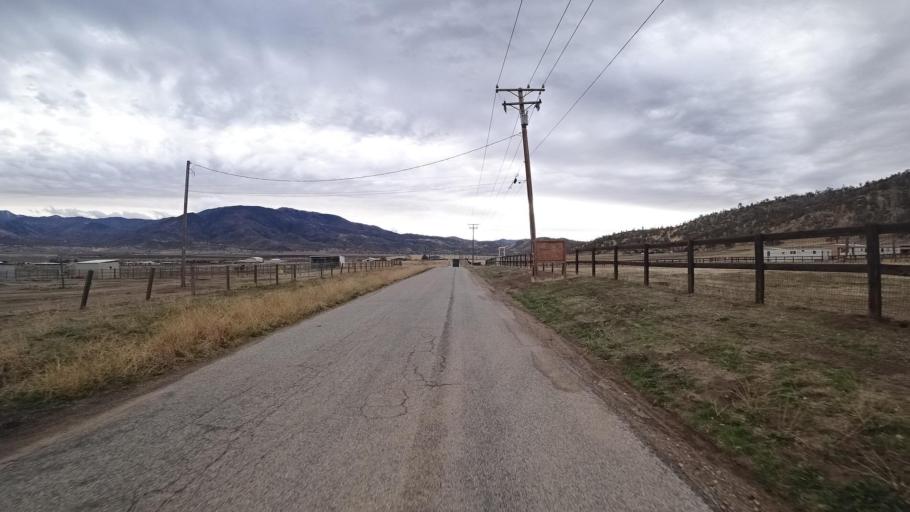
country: US
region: California
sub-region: Kern County
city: Stallion Springs
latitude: 35.1176
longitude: -118.6280
